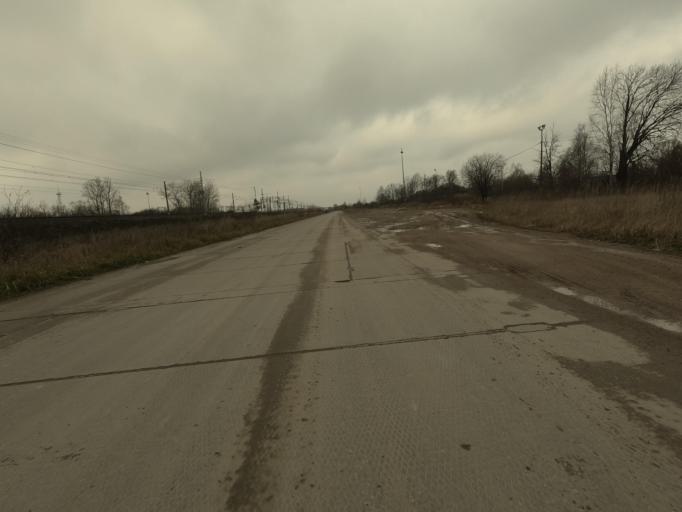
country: RU
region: Leningrad
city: Lyuban'
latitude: 59.4733
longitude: 31.2551
